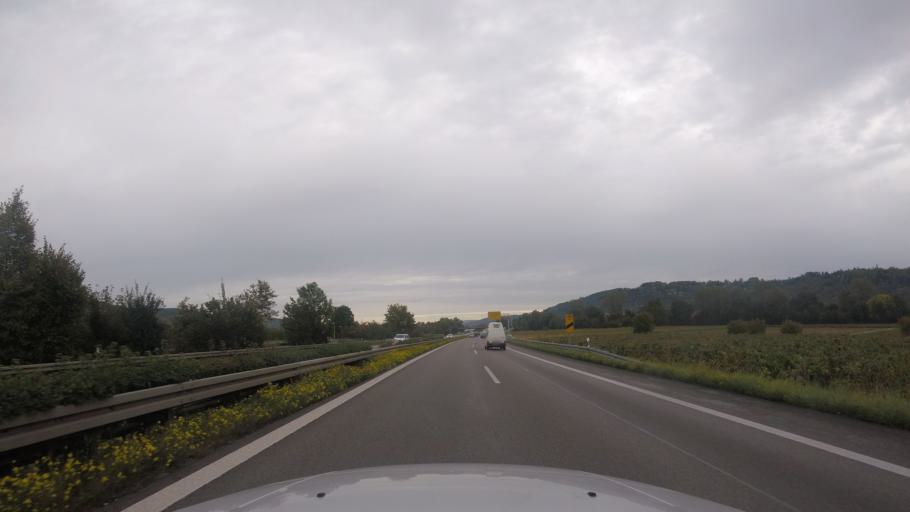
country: DE
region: Baden-Wuerttemberg
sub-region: Regierungsbezirk Stuttgart
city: Weinstadt-Endersbach
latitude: 48.8170
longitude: 9.4016
